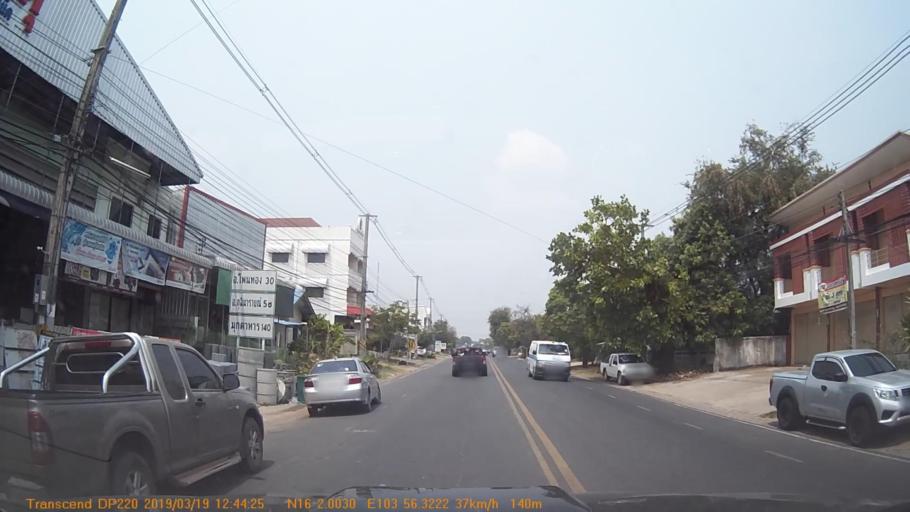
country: TH
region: Roi Et
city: Selaphum
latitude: 16.0336
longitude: 103.9387
